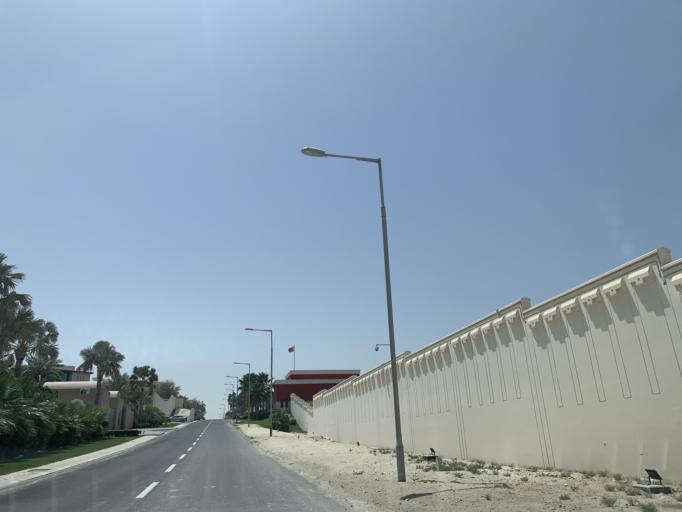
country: BH
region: Northern
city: Ar Rifa'
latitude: 26.1474
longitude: 50.5545
